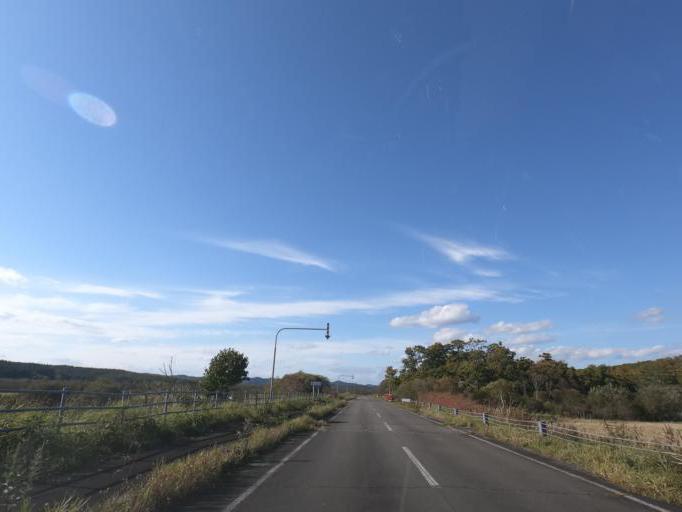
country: JP
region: Hokkaido
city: Obihiro
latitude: 42.6329
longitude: 143.5208
